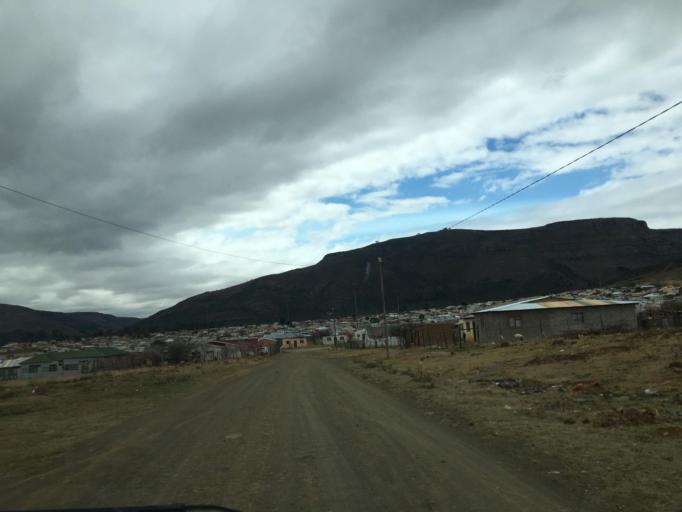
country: ZA
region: Eastern Cape
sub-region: Chris Hani District Municipality
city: Cala
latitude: -31.5396
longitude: 27.6983
